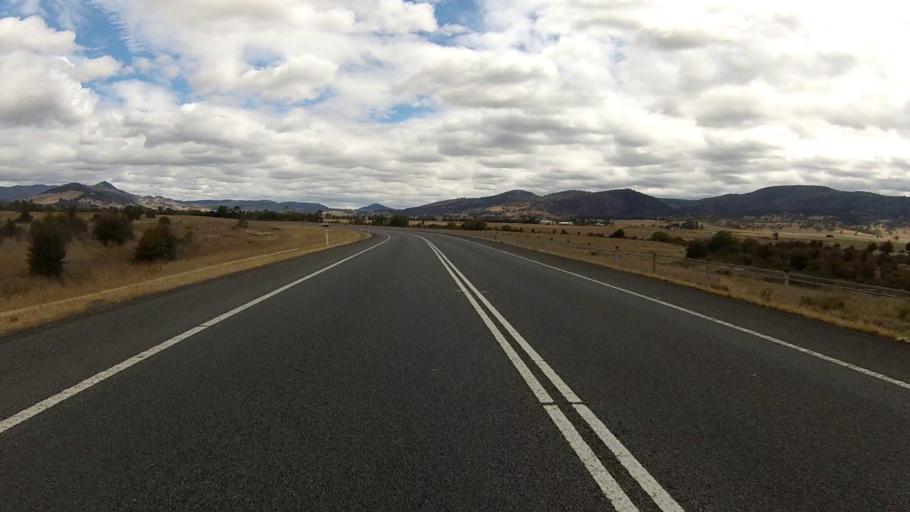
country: AU
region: Tasmania
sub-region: Brighton
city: Bridgewater
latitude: -42.6744
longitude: 147.2700
